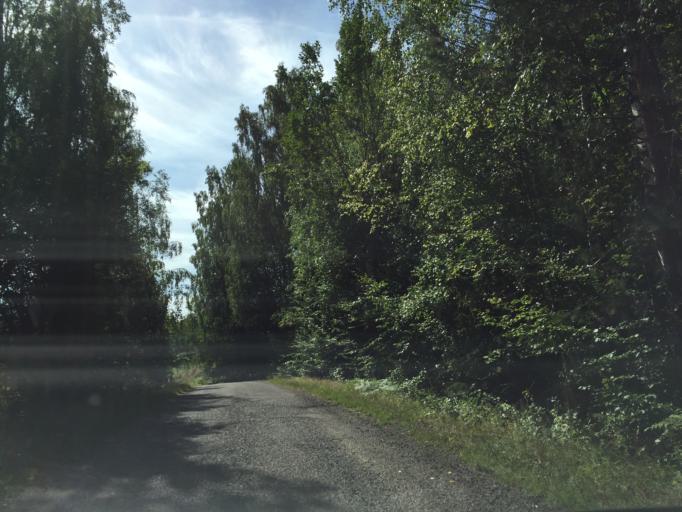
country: NO
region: Vestfold
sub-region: Hof
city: Hof
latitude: 59.4599
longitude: 10.1449
